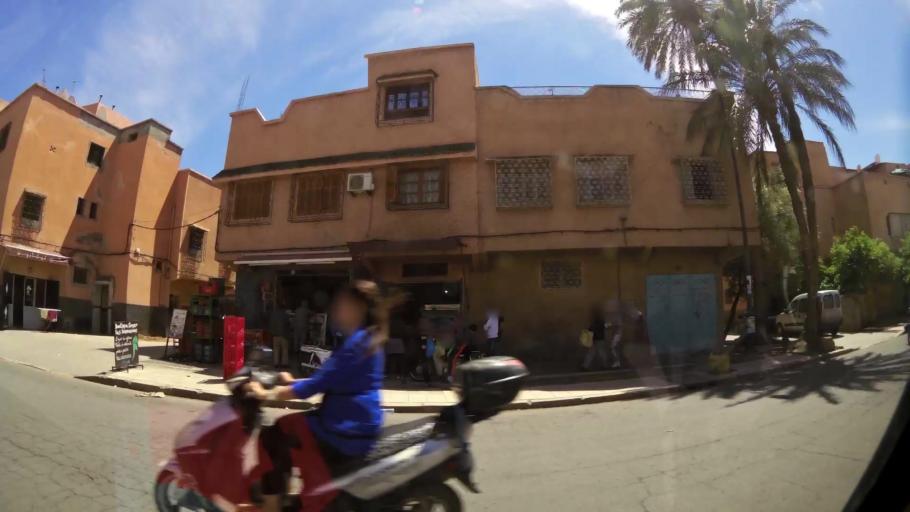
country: MA
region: Marrakech-Tensift-Al Haouz
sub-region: Marrakech
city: Marrakesh
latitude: 31.6536
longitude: -7.9912
